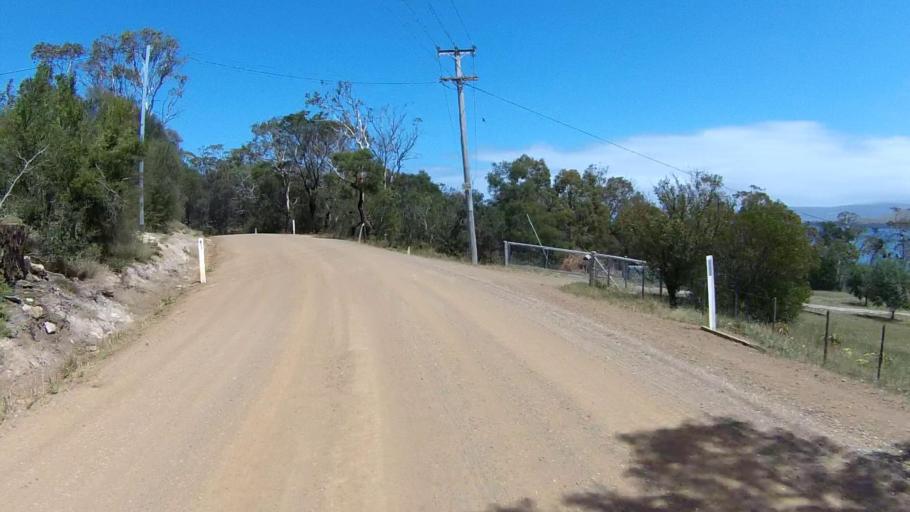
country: AU
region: Tasmania
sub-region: Clarence
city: Lauderdale
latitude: -42.9343
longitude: 147.4635
